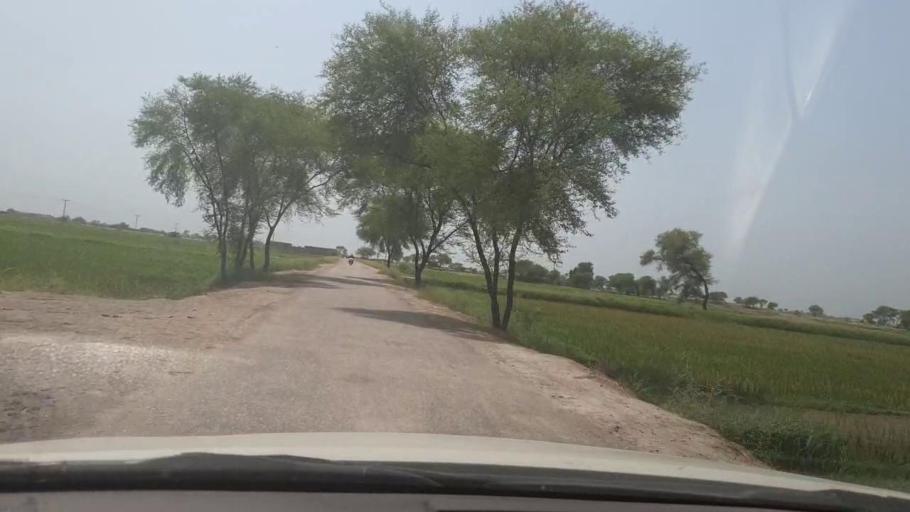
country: PK
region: Sindh
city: Shikarpur
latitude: 27.9936
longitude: 68.5773
